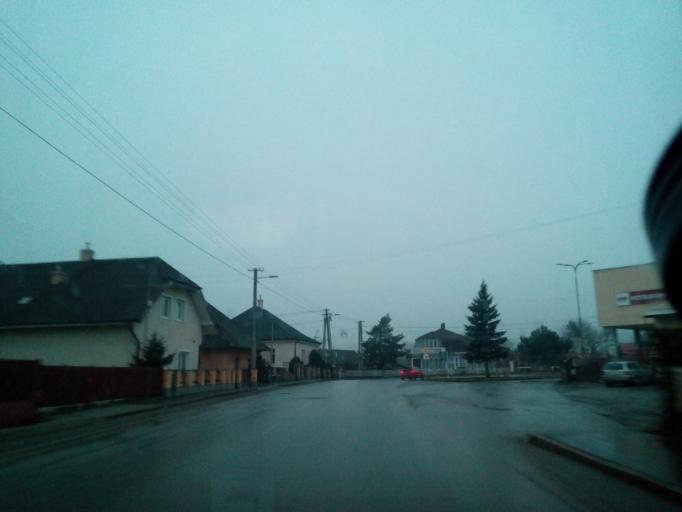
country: SK
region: Presovsky
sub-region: Okres Presov
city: Presov
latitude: 49.0397
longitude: 21.2003
